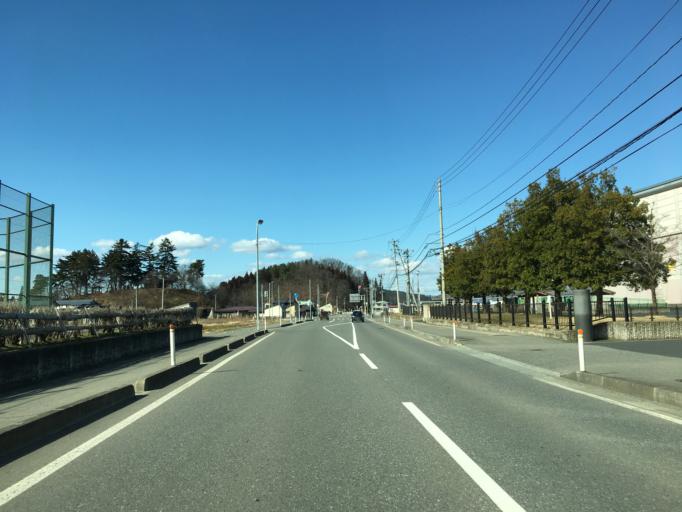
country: JP
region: Yamagata
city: Yonezawa
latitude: 37.9204
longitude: 140.1459
